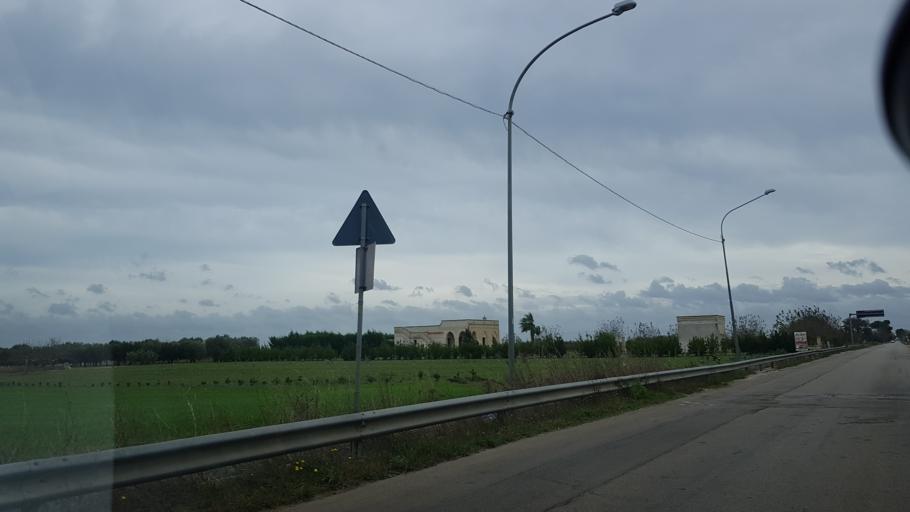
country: IT
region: Apulia
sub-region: Provincia di Brindisi
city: San Pancrazio Salentino
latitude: 40.4156
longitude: 17.8494
